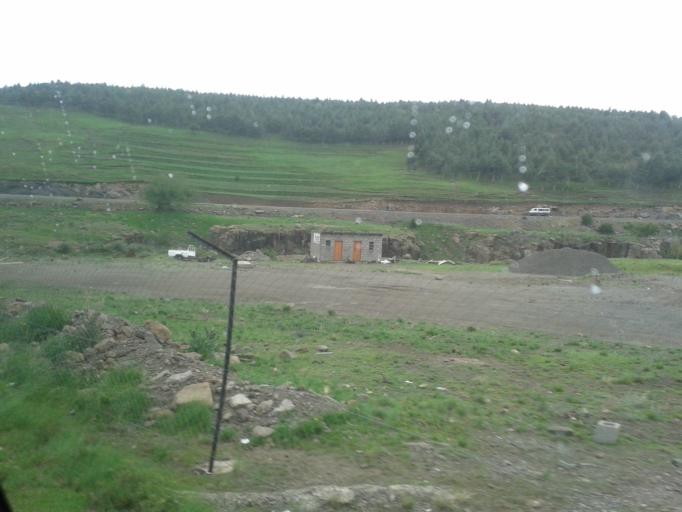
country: LS
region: Maseru
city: Nako
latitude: -29.8274
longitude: 28.0367
